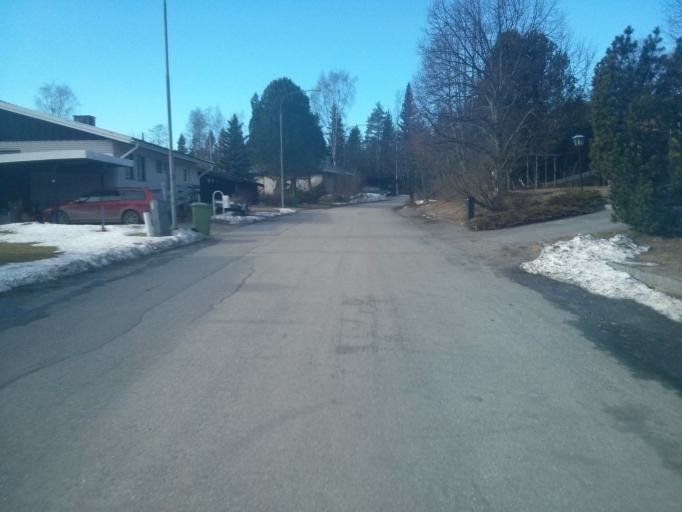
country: SE
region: Vaesternorrland
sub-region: Haernoesands Kommun
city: Haernoesand
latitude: 62.6433
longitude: 17.9233
